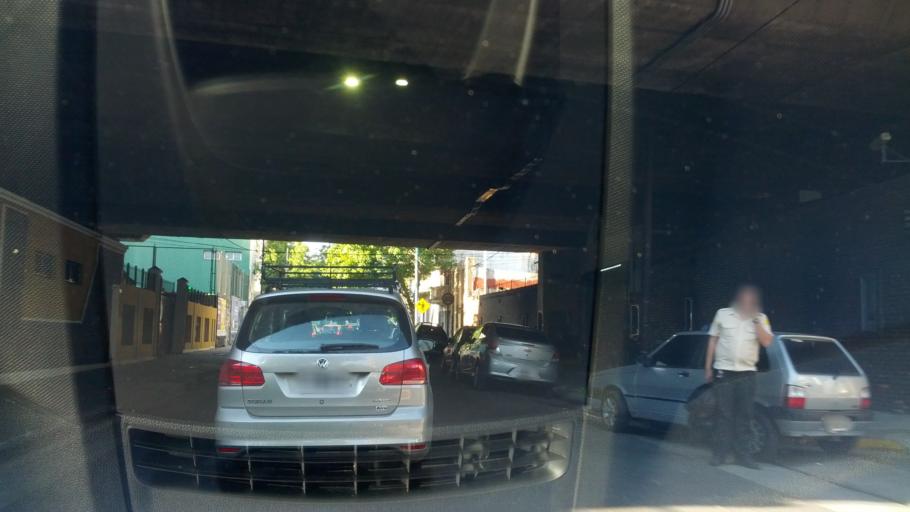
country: AR
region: Buenos Aires F.D.
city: Buenos Aires
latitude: -34.6235
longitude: -58.3872
